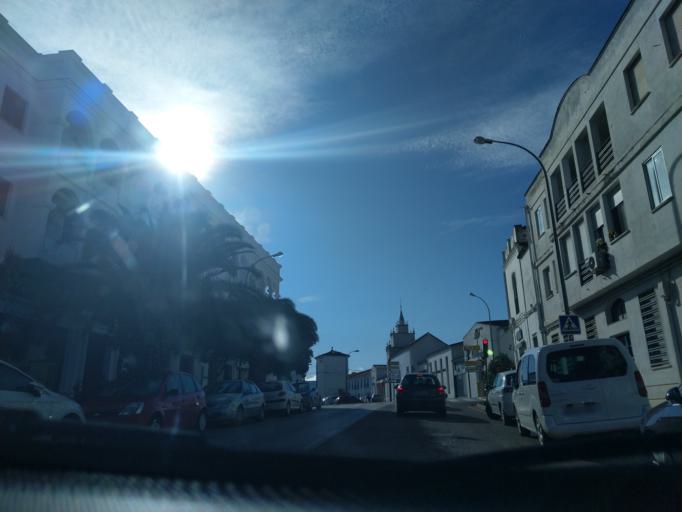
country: ES
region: Extremadura
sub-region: Provincia de Badajoz
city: Llerena
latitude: 38.2392
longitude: -6.0130
